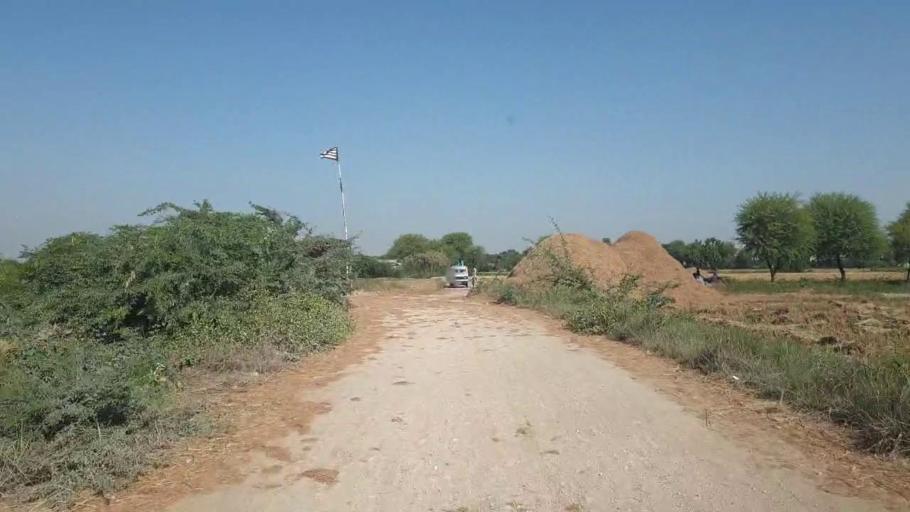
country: PK
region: Sindh
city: Talhar
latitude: 24.7941
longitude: 68.7962
